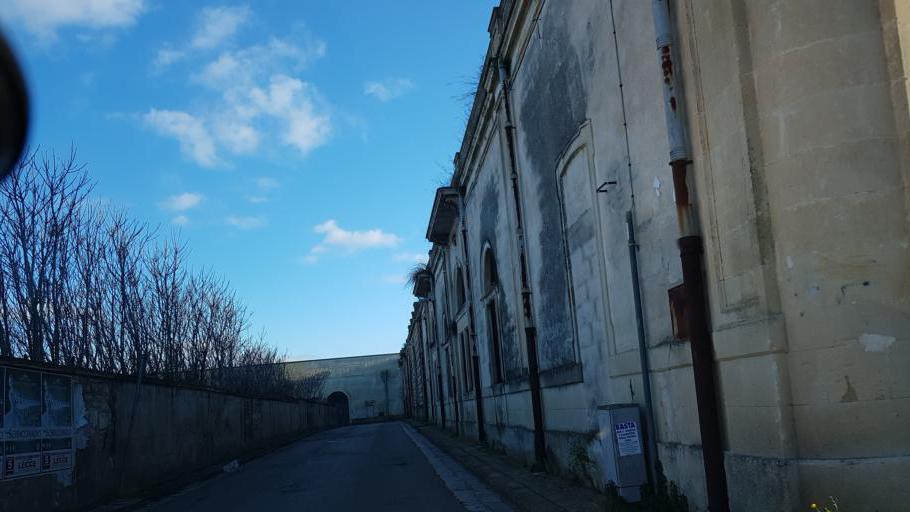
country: IT
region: Apulia
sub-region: Provincia di Lecce
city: Squinzano
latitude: 40.4405
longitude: 18.0437
